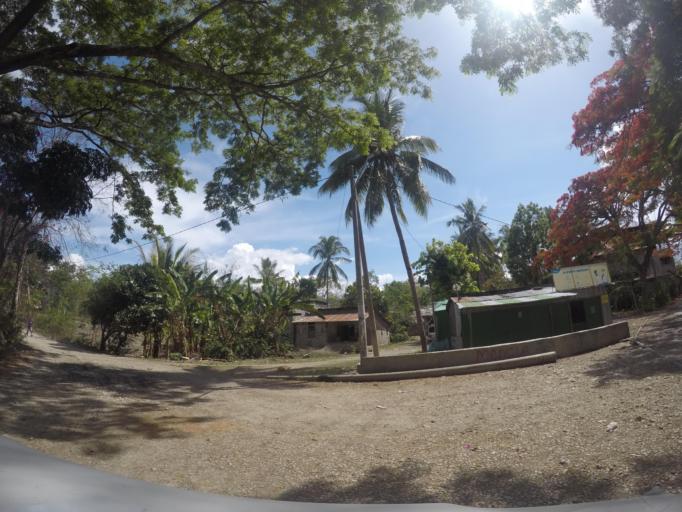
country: TL
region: Baucau
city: Baucau
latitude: -8.4676
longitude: 126.4605
